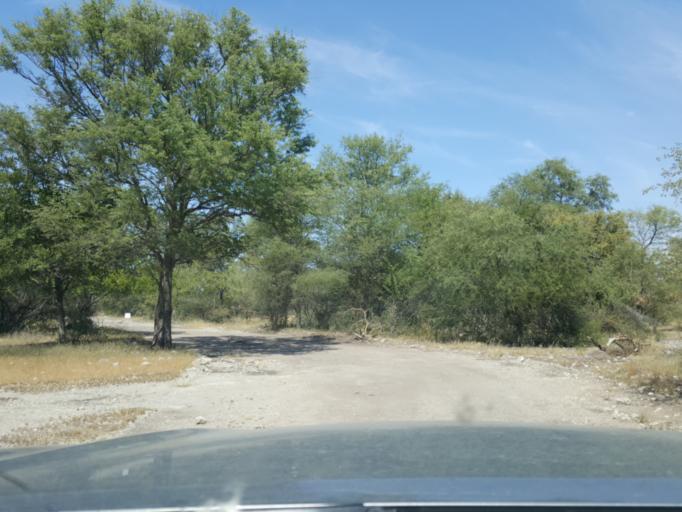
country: BW
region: North West
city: Shakawe
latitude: -18.7598
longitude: 21.7378
